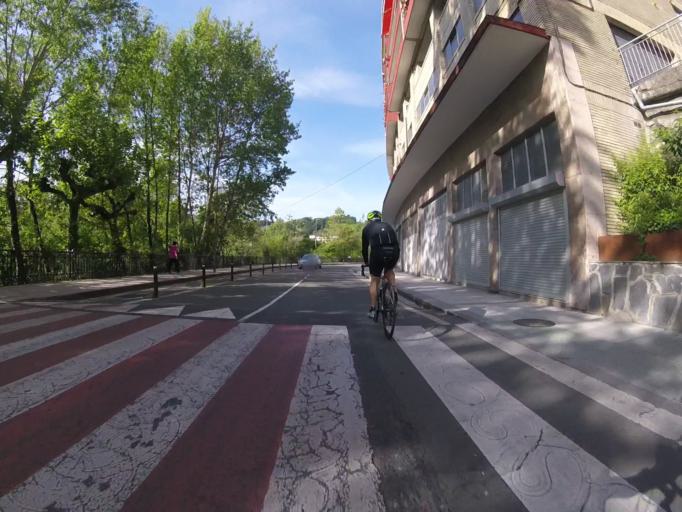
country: ES
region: Basque Country
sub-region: Provincia de Guipuzcoa
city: Beasain
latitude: 43.0489
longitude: -2.1912
